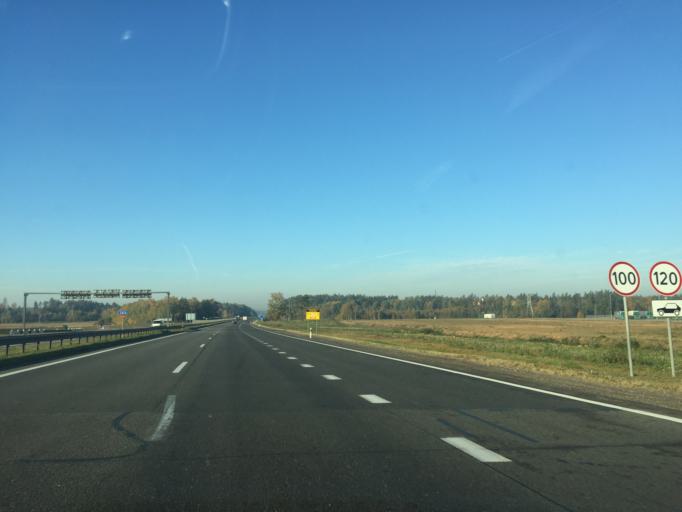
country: BY
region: Minsk
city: Pryvol'ny
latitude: 53.8024
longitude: 27.7857
